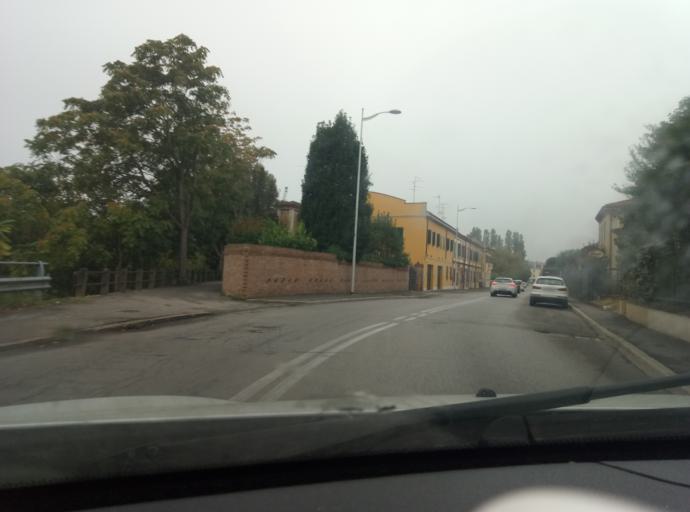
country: IT
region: Emilia-Romagna
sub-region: Provincia di Ferrara
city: Ferrara
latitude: 44.8308
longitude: 11.6141
